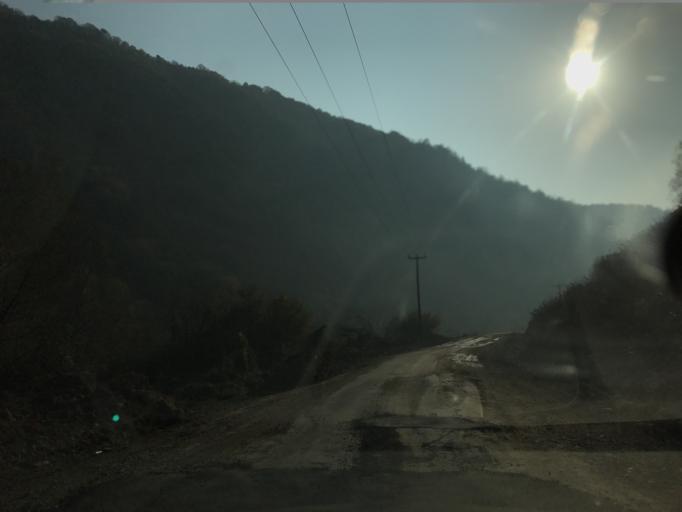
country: TR
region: Duzce
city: Cumayeri
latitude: 40.9283
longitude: 30.9287
